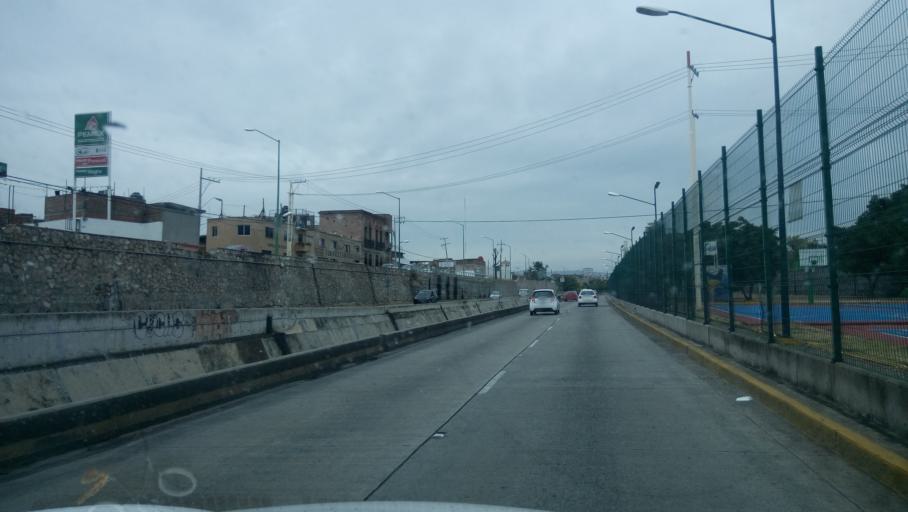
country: MX
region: Guanajuato
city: Leon
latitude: 21.1274
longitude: -101.6759
